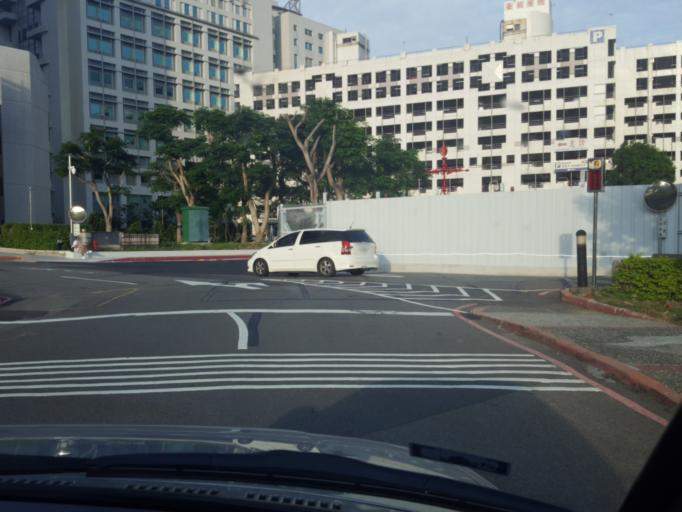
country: TW
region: Taipei
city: Taipei
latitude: 25.1190
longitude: 121.5202
